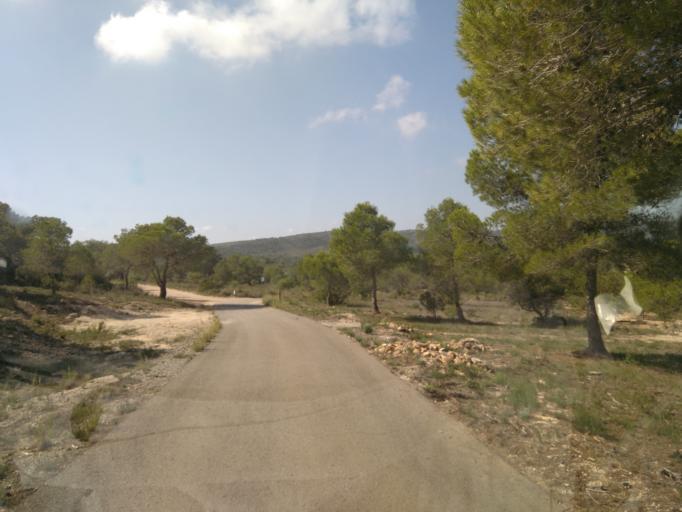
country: ES
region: Valencia
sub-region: Provincia de Valencia
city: Tous
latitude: 39.1752
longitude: -0.6147
